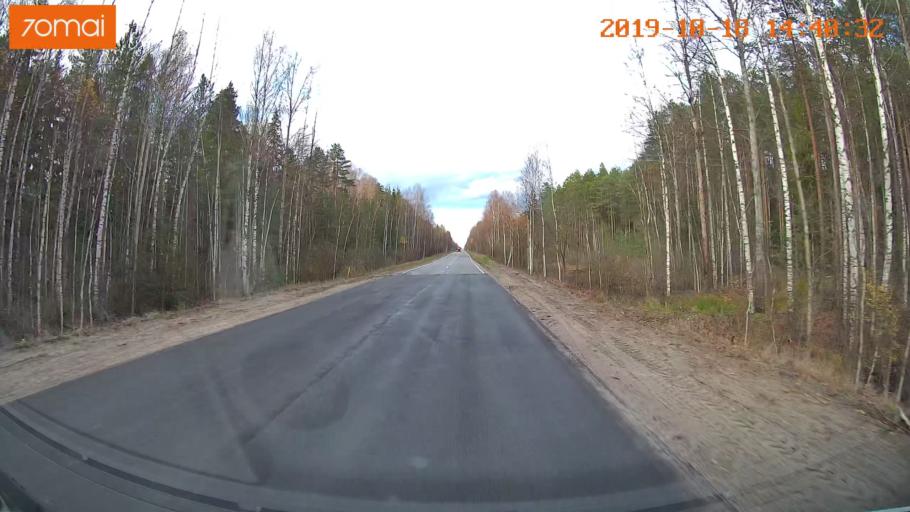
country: RU
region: Vladimir
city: Velikodvorskiy
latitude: 55.2781
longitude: 40.6692
